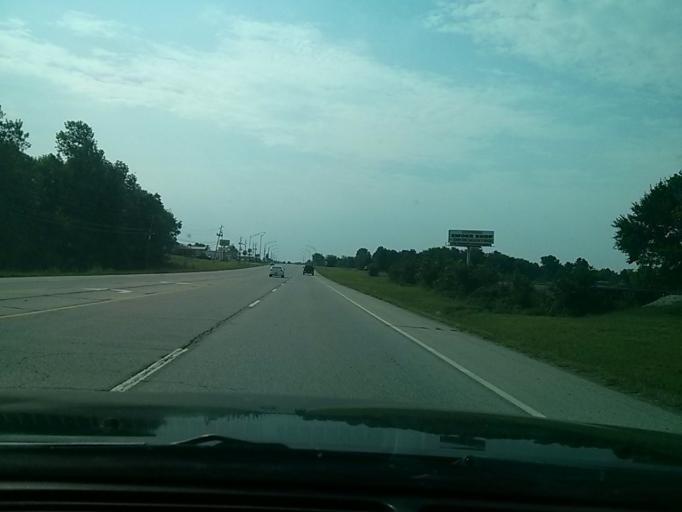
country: US
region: Oklahoma
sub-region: Wagoner County
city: Coweta
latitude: 35.9713
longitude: -95.6600
